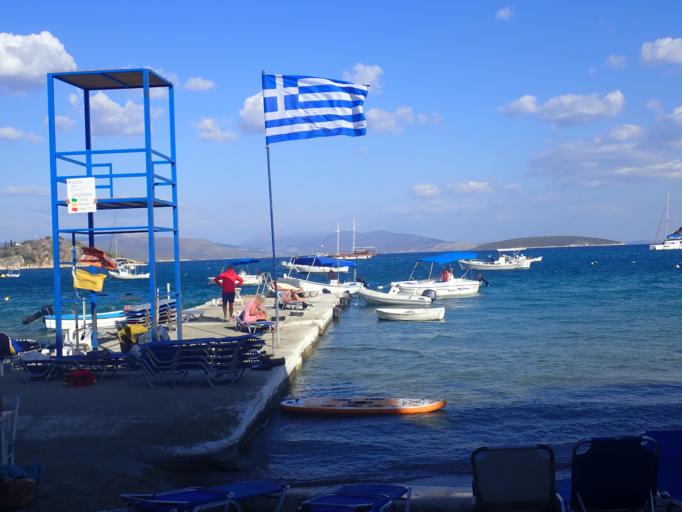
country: GR
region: Peloponnese
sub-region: Nomos Argolidos
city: Tolon
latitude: 37.5178
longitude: 22.8585
